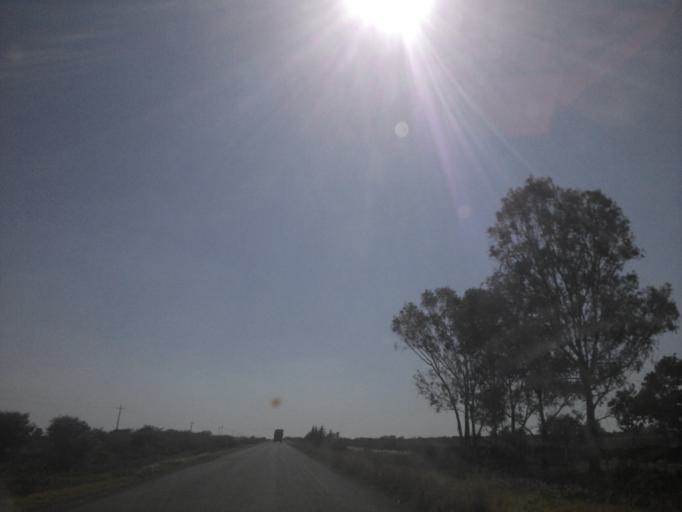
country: MX
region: Jalisco
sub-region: Arandas
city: Santiaguito (Santiaguito de Velazquez)
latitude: 20.8238
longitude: -102.1748
